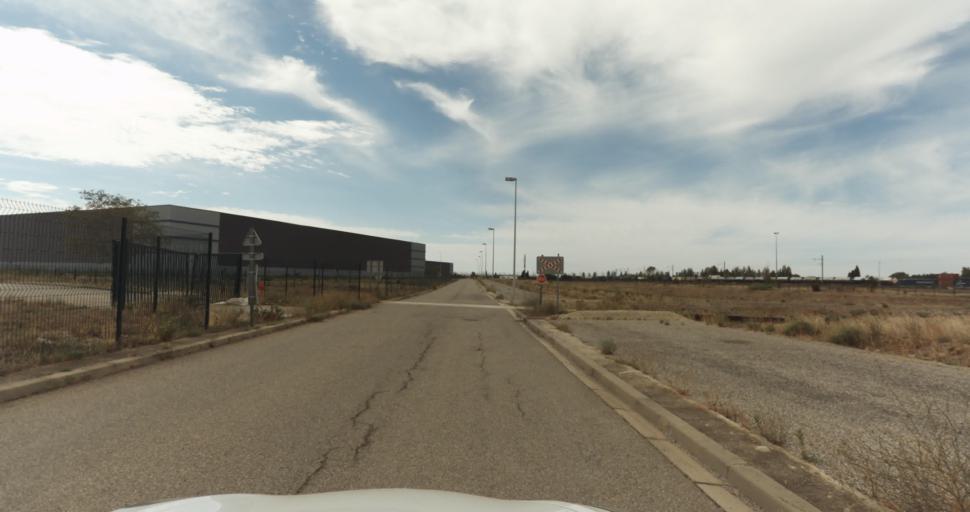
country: FR
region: Provence-Alpes-Cote d'Azur
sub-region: Departement des Bouches-du-Rhone
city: Miramas
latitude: 43.6064
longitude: 4.9920
